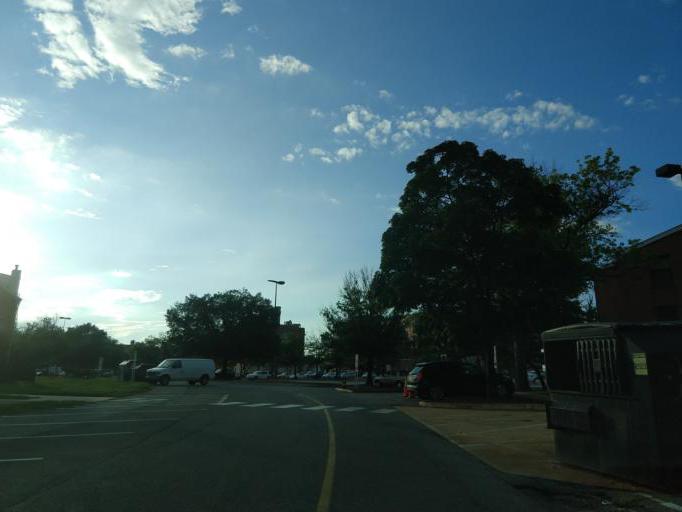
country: US
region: Maryland
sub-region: Prince George's County
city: College Park
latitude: 38.9844
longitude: -76.9339
